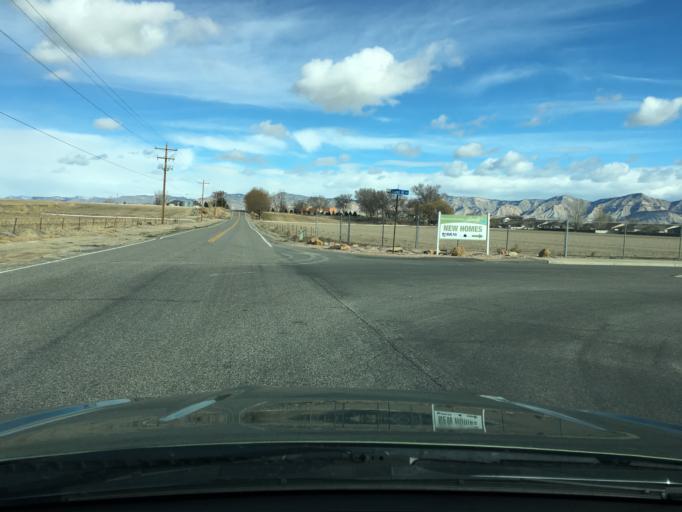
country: US
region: Colorado
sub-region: Mesa County
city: Grand Junction
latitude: 39.1279
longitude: -108.5616
